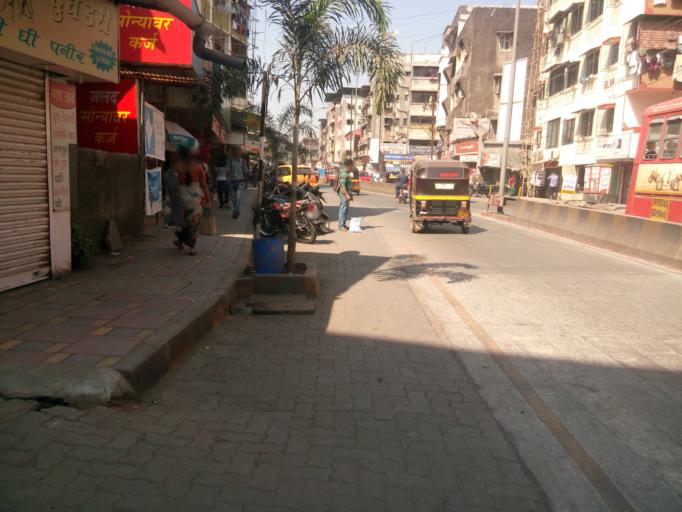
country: IN
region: Maharashtra
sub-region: Thane
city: Dombivli
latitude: 19.2091
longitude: 73.0941
